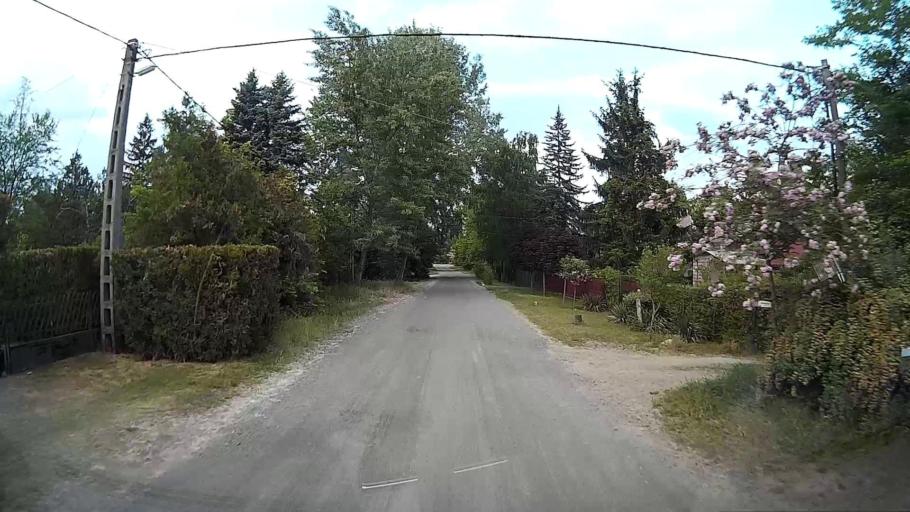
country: HU
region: Pest
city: God
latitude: 47.6765
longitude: 19.1153
